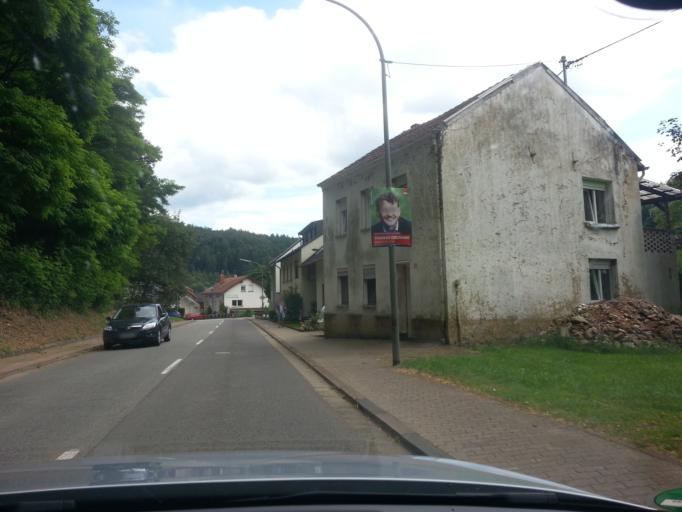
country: DE
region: Saarland
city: Beckingen
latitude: 49.4304
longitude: 6.7278
